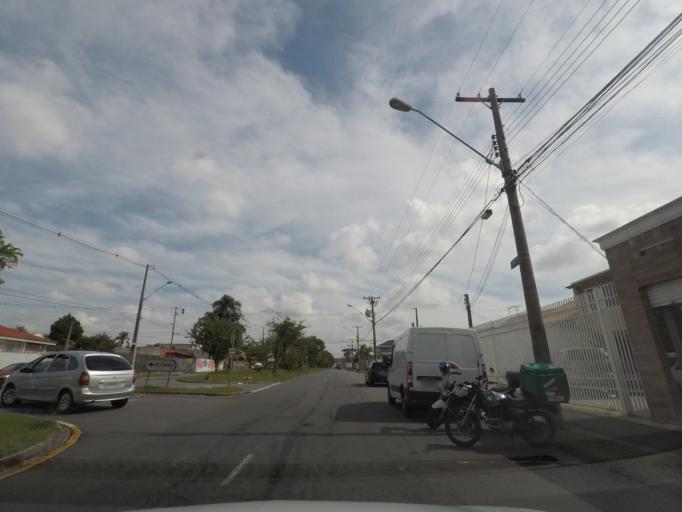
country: BR
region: Parana
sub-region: Pinhais
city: Pinhais
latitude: -25.4716
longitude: -49.2069
